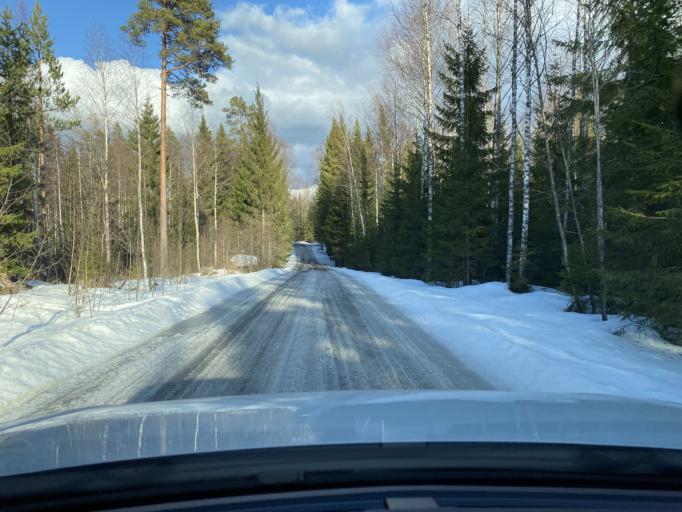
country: FI
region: Pirkanmaa
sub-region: Lounais-Pirkanmaa
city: Mouhijaervi
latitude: 61.4610
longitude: 22.9555
